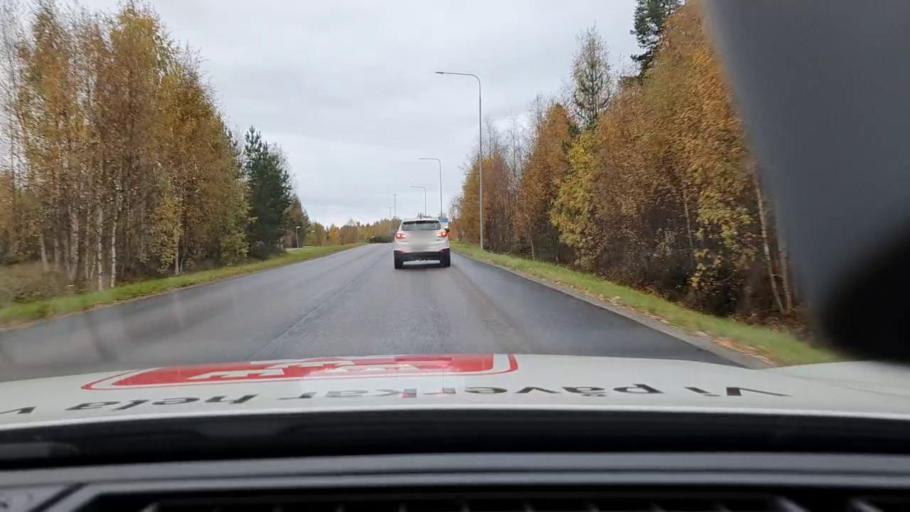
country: SE
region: Norrbotten
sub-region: Bodens Kommun
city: Saevast
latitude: 65.7643
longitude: 21.7388
